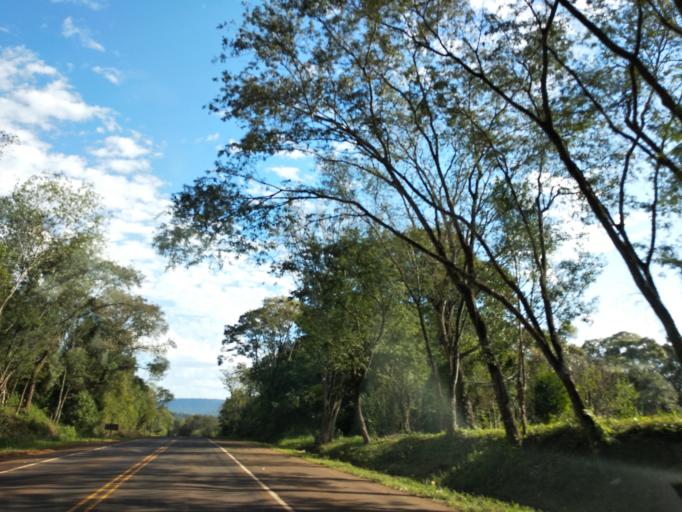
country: AR
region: Misiones
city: Aristobulo del Valle
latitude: -27.0978
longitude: -54.9577
